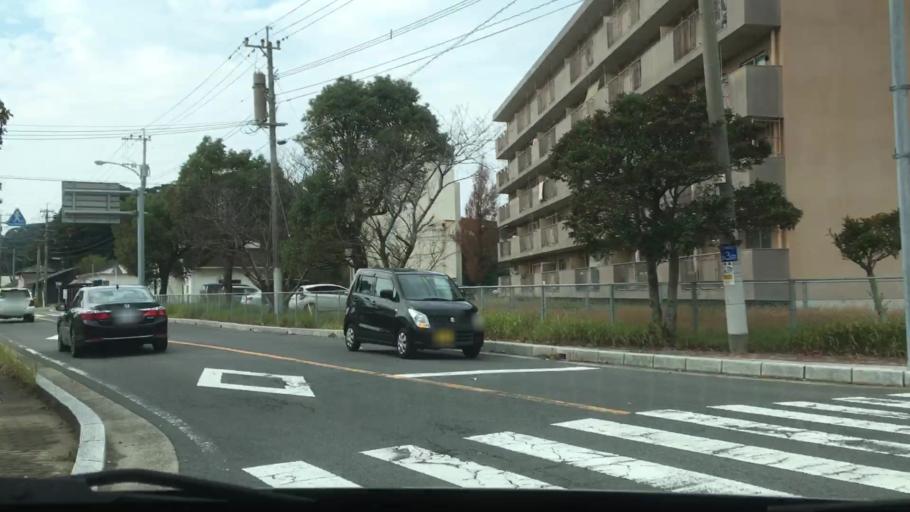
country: JP
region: Nagasaki
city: Sasebo
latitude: 33.0378
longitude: 129.6255
